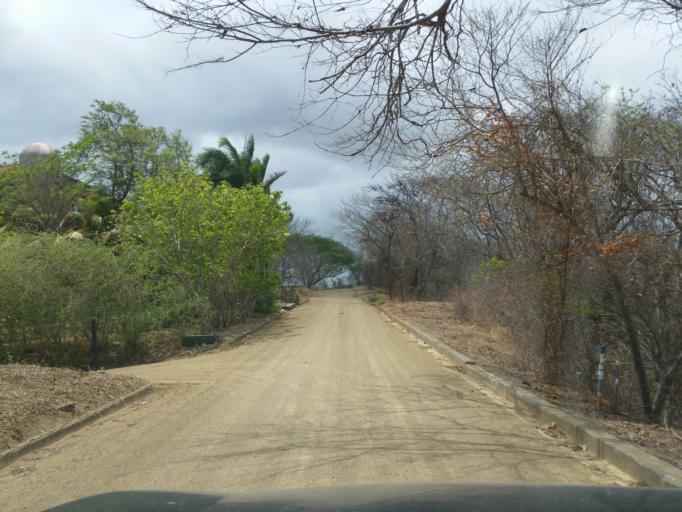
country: NI
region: Rivas
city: Tola
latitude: 11.4380
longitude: -86.0825
